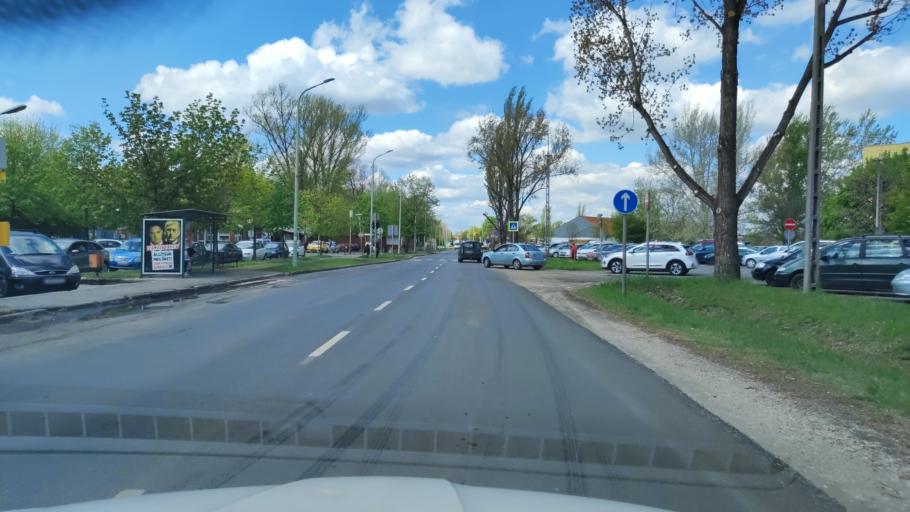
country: HU
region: Pest
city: Cegled
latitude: 47.1716
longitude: 19.8187
